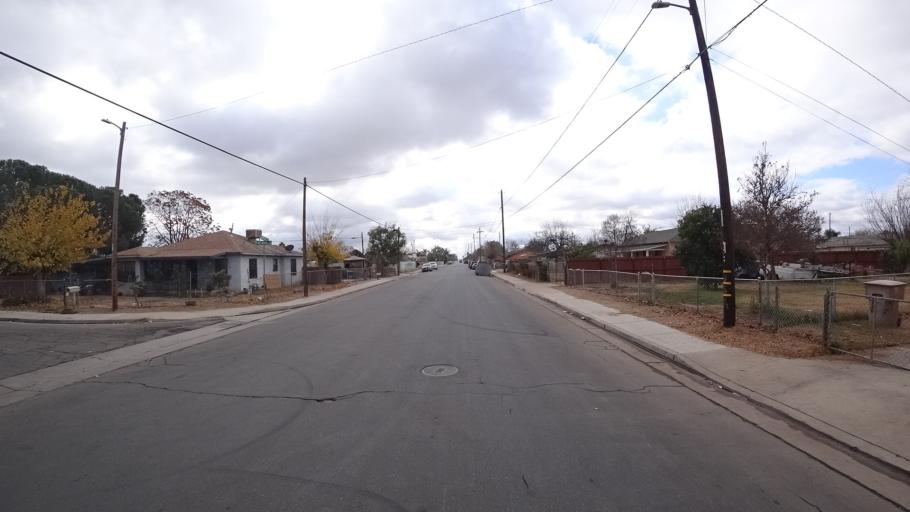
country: US
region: California
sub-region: Kern County
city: Bakersfield
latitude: 35.3334
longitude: -118.9899
